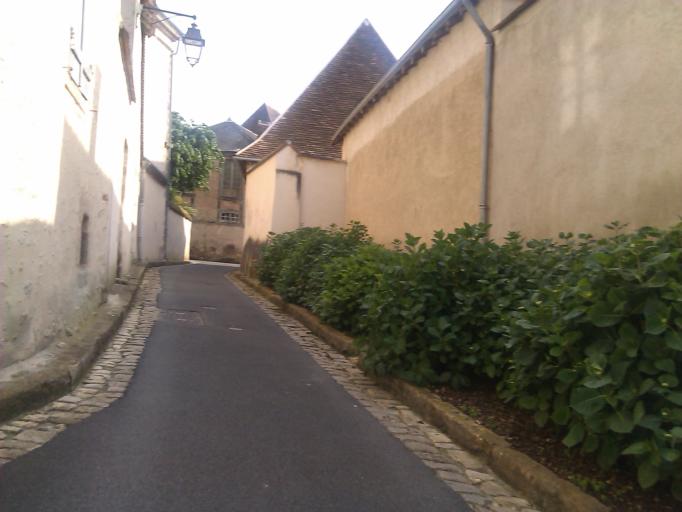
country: FR
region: Centre
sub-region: Departement de l'Indre
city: La Chatre
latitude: 46.5819
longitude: 1.9889
